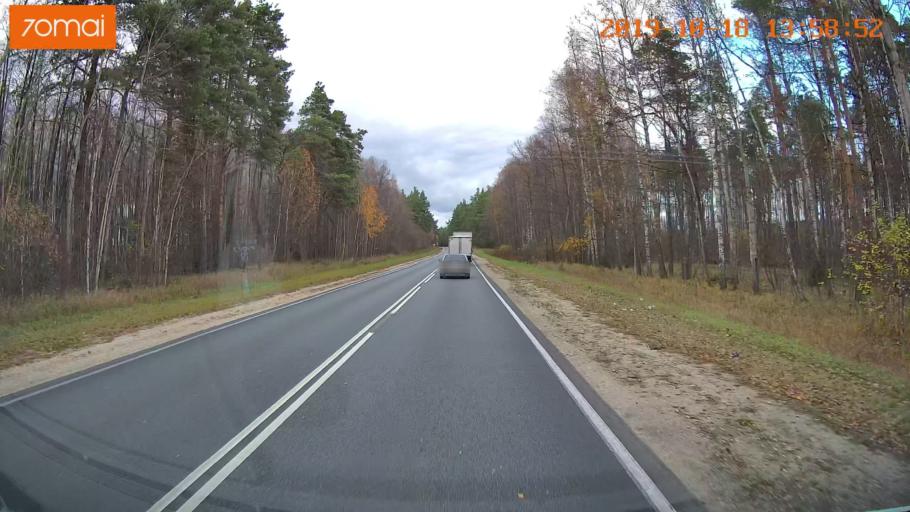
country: RU
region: Rjazan
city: Spas-Klepiki
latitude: 55.0892
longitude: 40.0578
